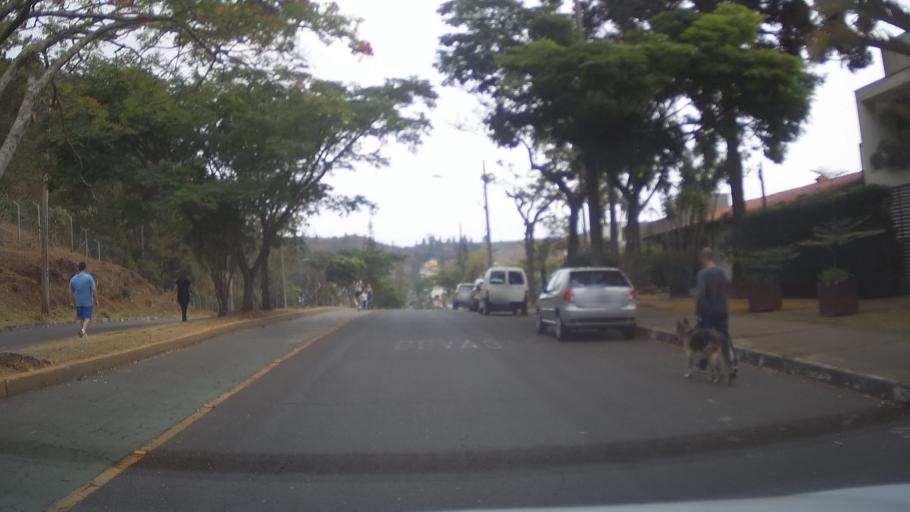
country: BR
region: Minas Gerais
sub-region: Belo Horizonte
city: Belo Horizonte
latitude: -19.9569
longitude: -43.9105
